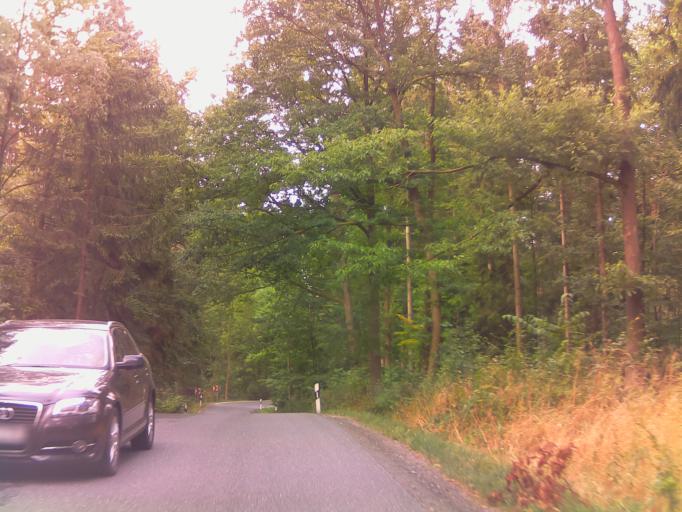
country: DE
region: Thuringia
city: Burgk
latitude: 50.5425
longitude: 11.7153
